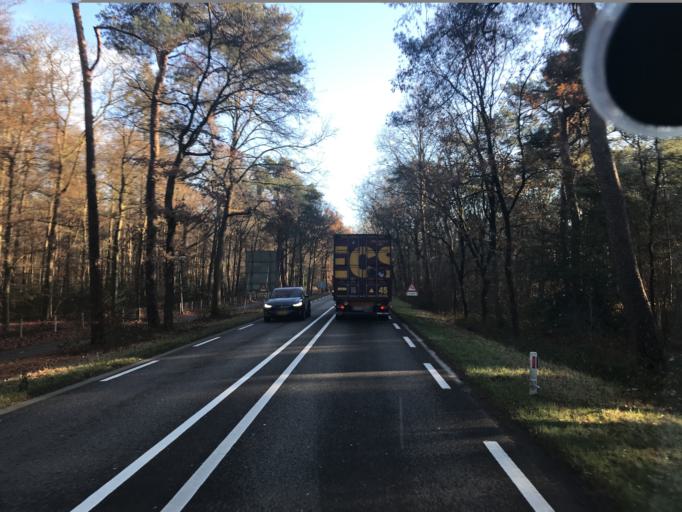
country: NL
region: Gelderland
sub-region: Gemeente Harderwijk
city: Harderwijk
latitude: 52.3303
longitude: 5.6418
